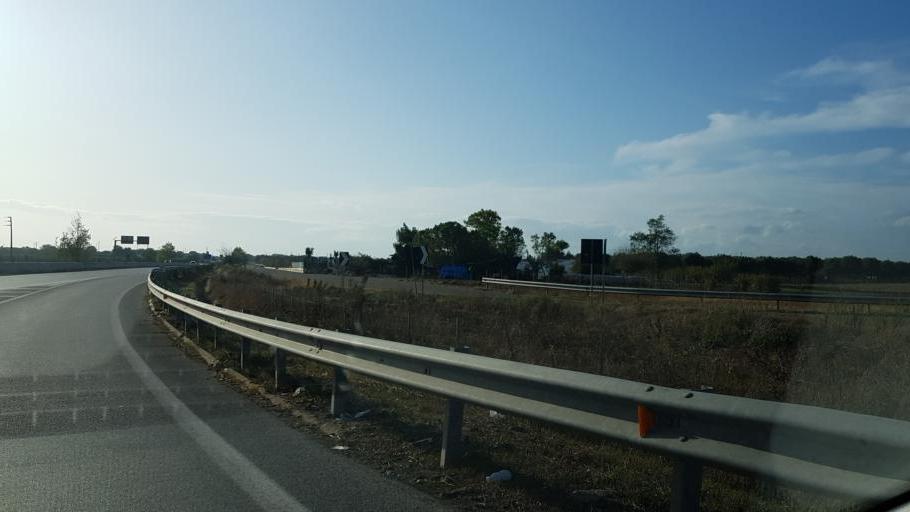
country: IT
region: Apulia
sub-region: Provincia di Brindisi
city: Oria
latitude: 40.5386
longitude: 17.6540
